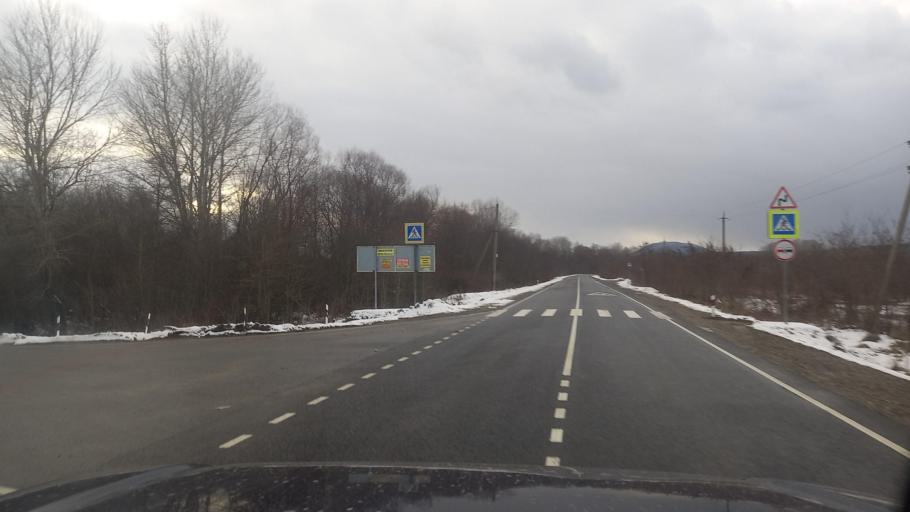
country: RU
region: Krasnodarskiy
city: Smolenskaya
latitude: 44.7422
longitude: 38.7437
